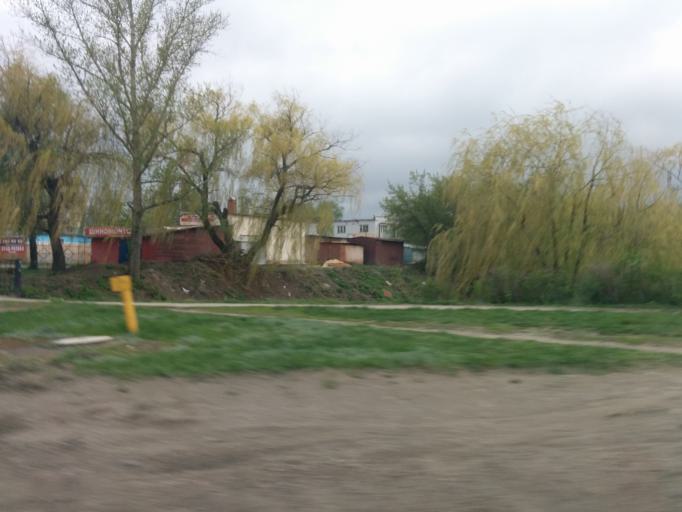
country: RU
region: Tambov
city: Tambov
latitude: 52.7277
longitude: 41.4353
